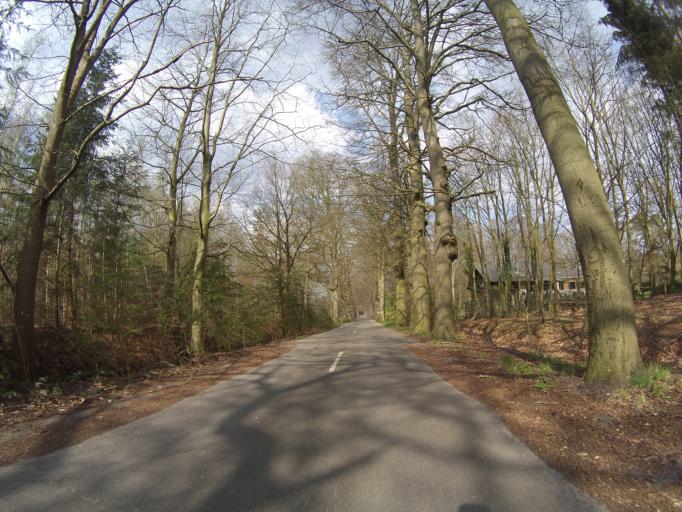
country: NL
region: Utrecht
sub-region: Gemeente De Bilt
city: De Bilt
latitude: 52.1614
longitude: 5.2238
